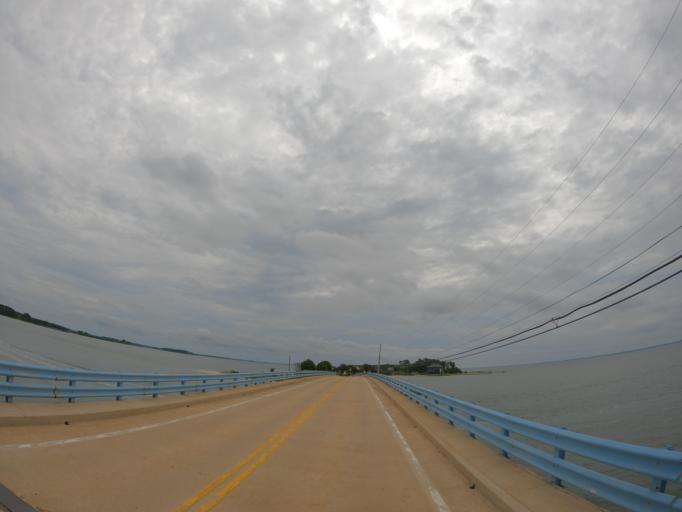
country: US
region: Maryland
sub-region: Saint Mary's County
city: Lexington Park
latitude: 38.1370
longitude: -76.4996
